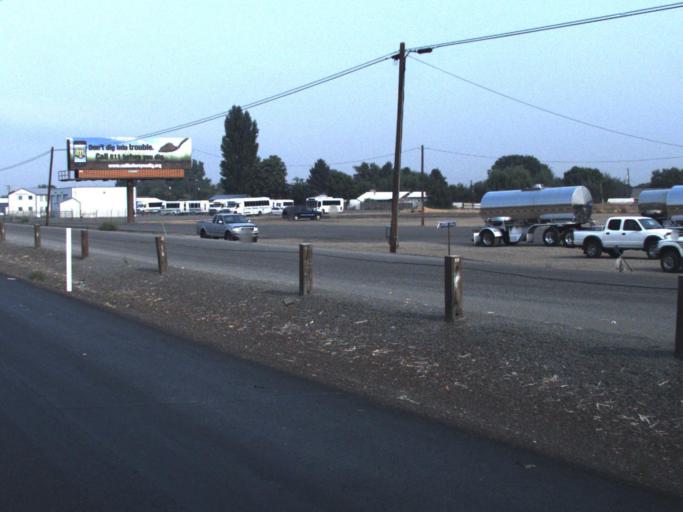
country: US
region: Washington
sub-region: Yakima County
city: Toppenish
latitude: 46.3872
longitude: -120.3534
